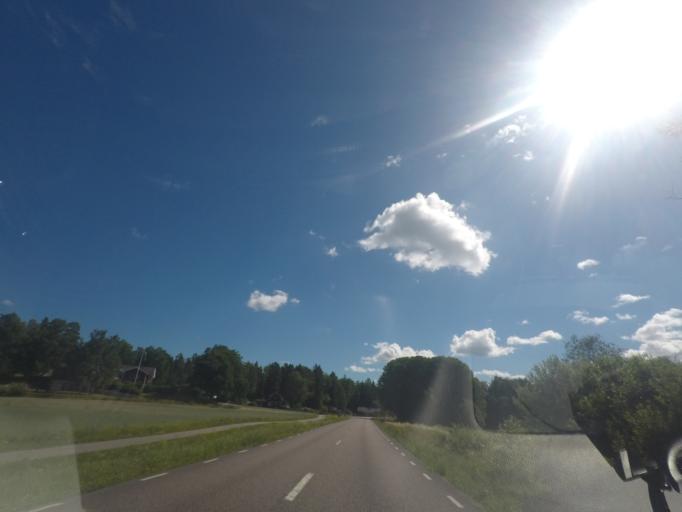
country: SE
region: Stockholm
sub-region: Norrtalje Kommun
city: Nykvarn
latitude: 59.8774
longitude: 18.0328
